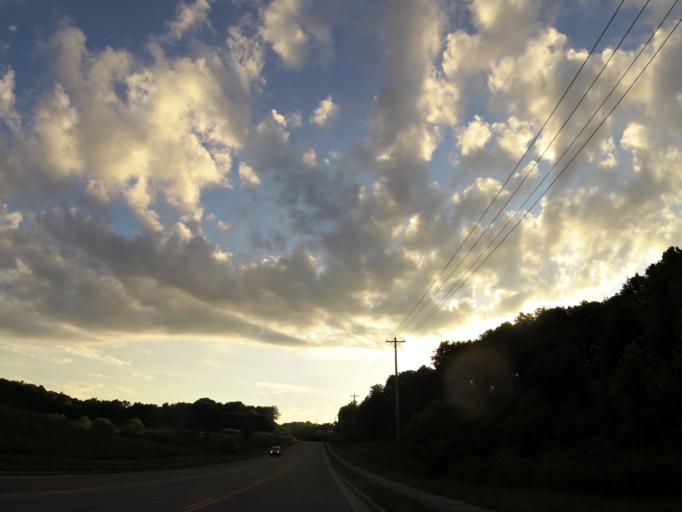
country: US
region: Tennessee
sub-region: Knox County
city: Farragut
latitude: 35.9039
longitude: -84.1605
